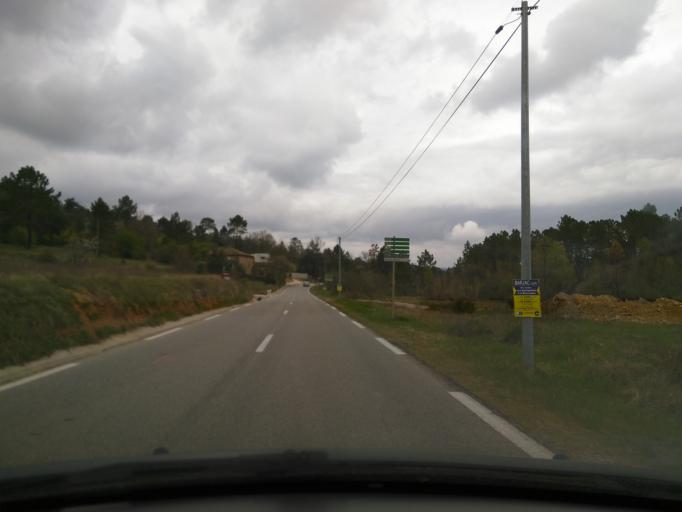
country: FR
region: Languedoc-Roussillon
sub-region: Departement du Gard
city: Barjac
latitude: 44.3731
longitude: 4.3708
